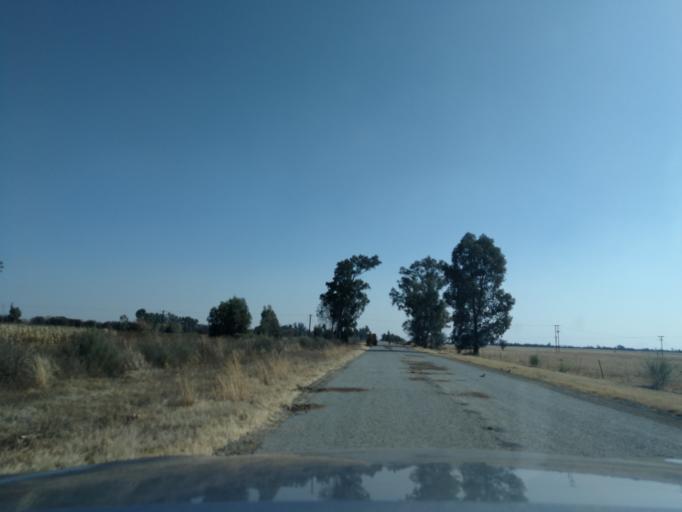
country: ZA
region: Orange Free State
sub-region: Fezile Dabi District Municipality
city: Viljoenskroon
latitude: -27.3455
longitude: 27.0052
